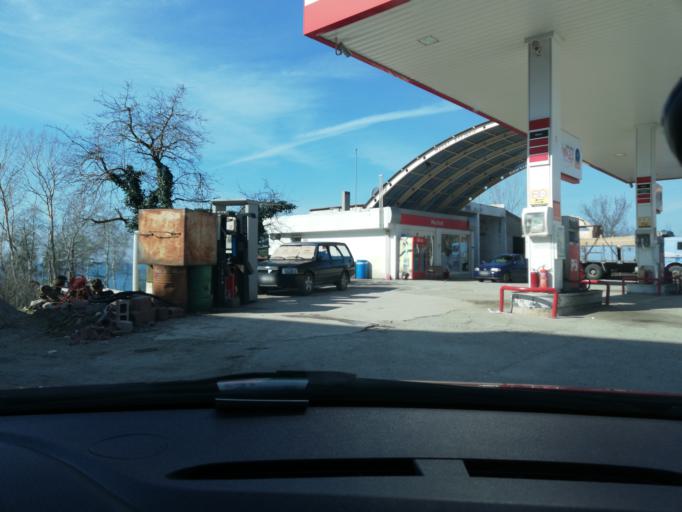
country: TR
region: Bartin
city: Kurucasile
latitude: 41.8448
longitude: 32.7160
